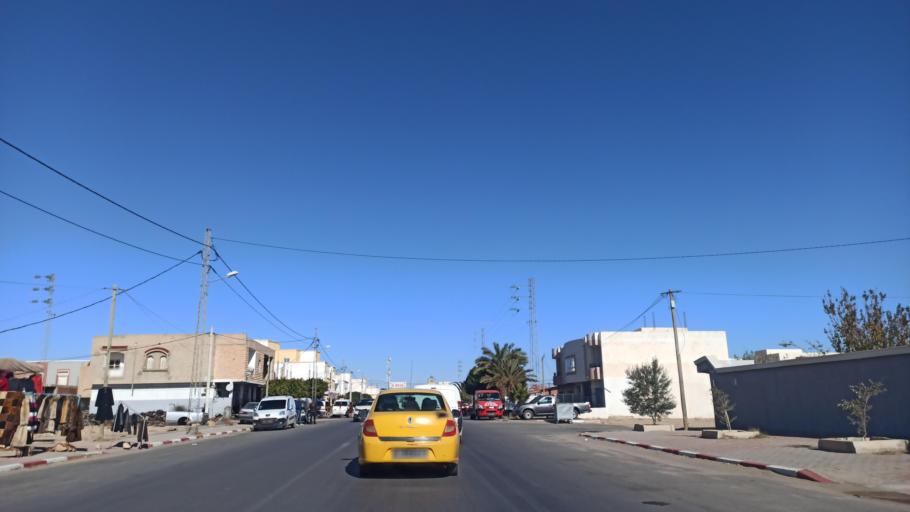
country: TN
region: Sidi Bu Zayd
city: Bi'r al Hufayy
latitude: 34.9228
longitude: 9.1890
